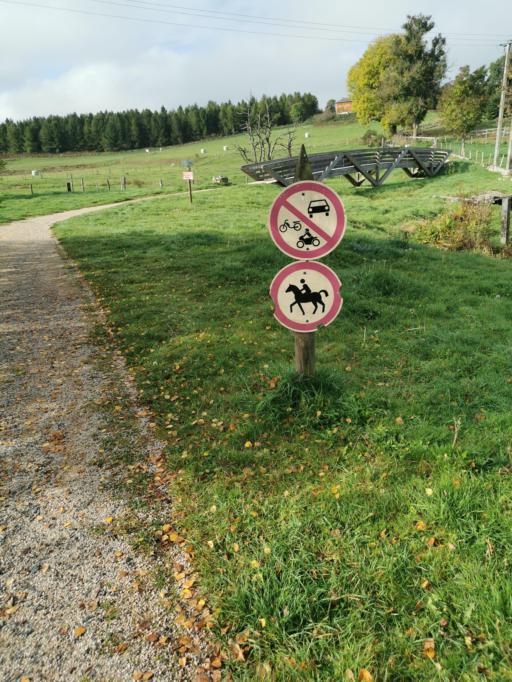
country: FR
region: Rhone-Alpes
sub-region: Departement de la Loire
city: Usson-en-Forez
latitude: 45.3896
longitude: 3.9515
